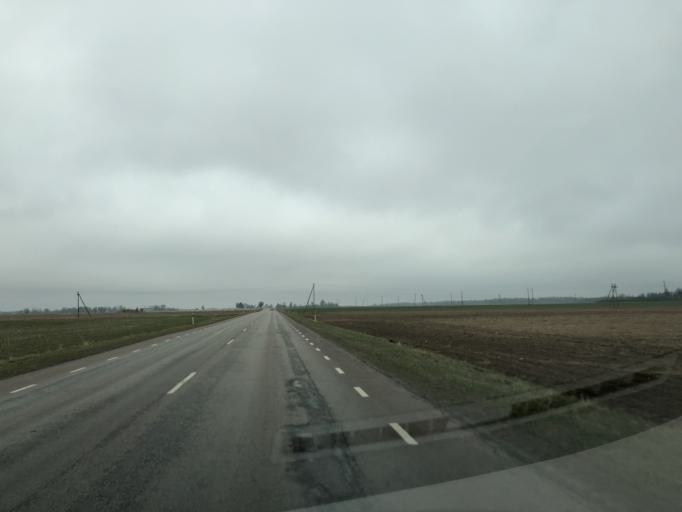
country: EE
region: Laeaene-Virumaa
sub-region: Vaeike-Maarja vald
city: Vaike-Maarja
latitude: 59.1641
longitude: 26.2665
